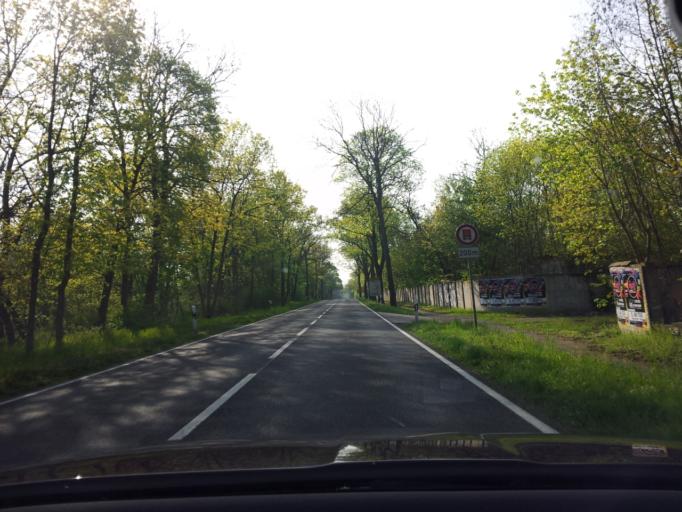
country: DE
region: Brandenburg
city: Niedergorsdorf
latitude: 52.0013
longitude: 13.0271
